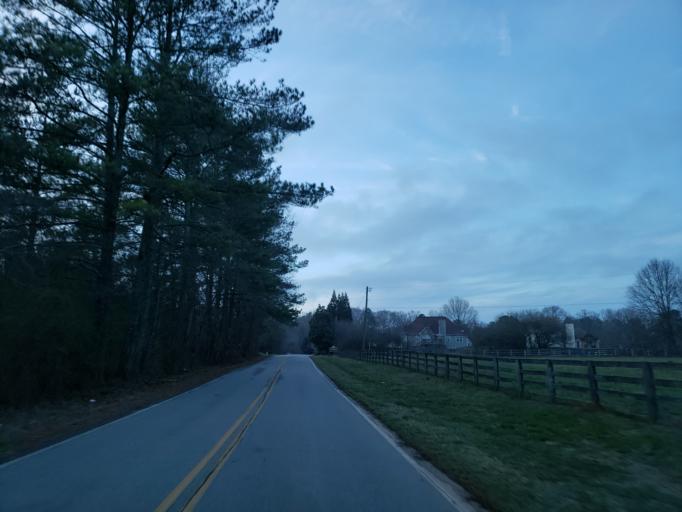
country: US
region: Georgia
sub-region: Cherokee County
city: Ball Ground
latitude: 34.2508
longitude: -84.3369
